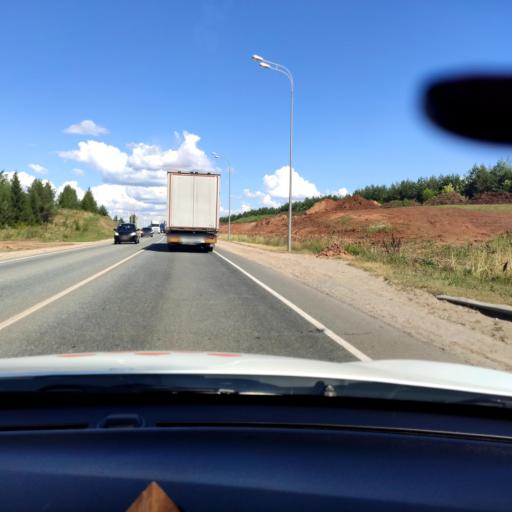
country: RU
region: Tatarstan
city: Sviyazhsk
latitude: 55.7299
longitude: 48.7678
